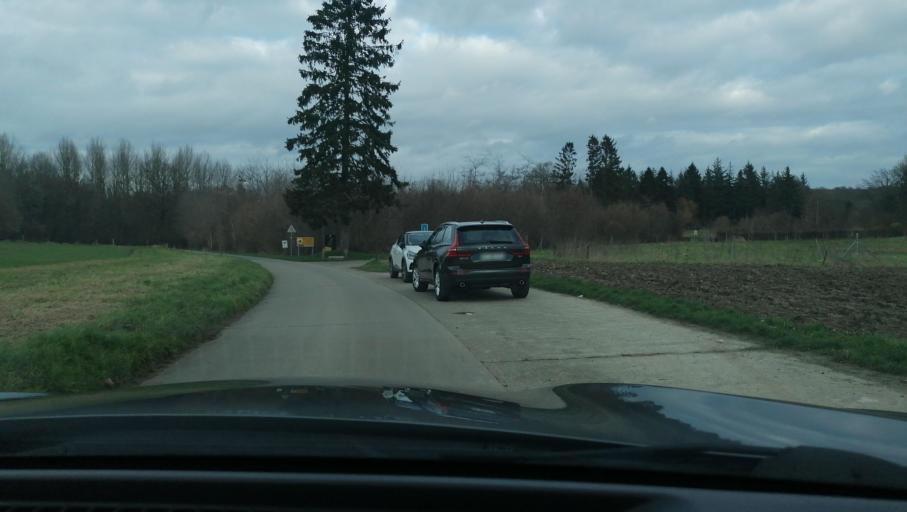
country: FR
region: Nord-Pas-de-Calais
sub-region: Departement du Nord
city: Wargnies-le-Grand
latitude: 50.3439
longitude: 3.7030
